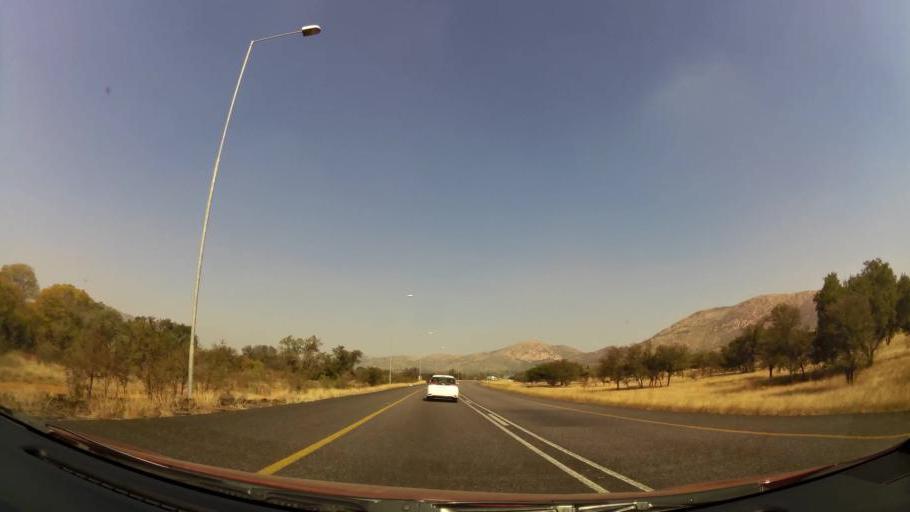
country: ZA
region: North-West
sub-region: Bojanala Platinum District Municipality
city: Rustenburg
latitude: -25.6265
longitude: 27.1579
